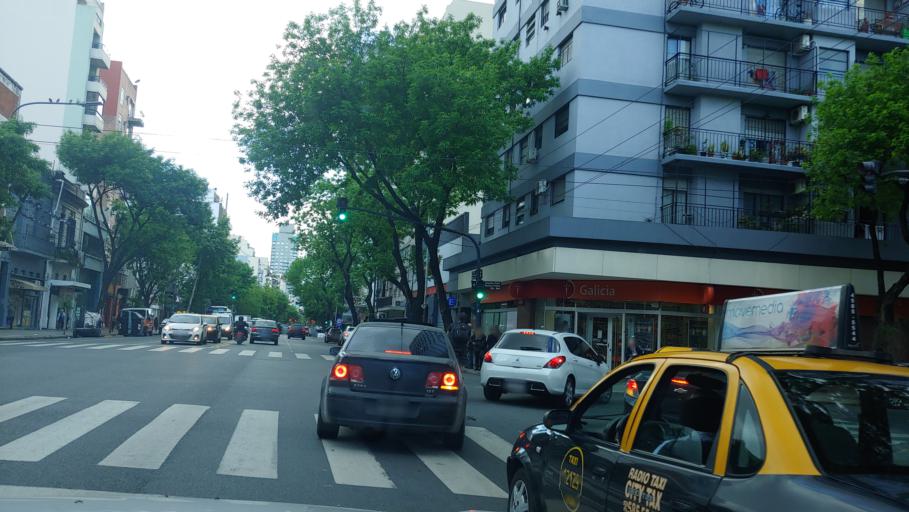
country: AR
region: Buenos Aires F.D.
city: Colegiales
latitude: -34.5769
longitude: -58.4488
